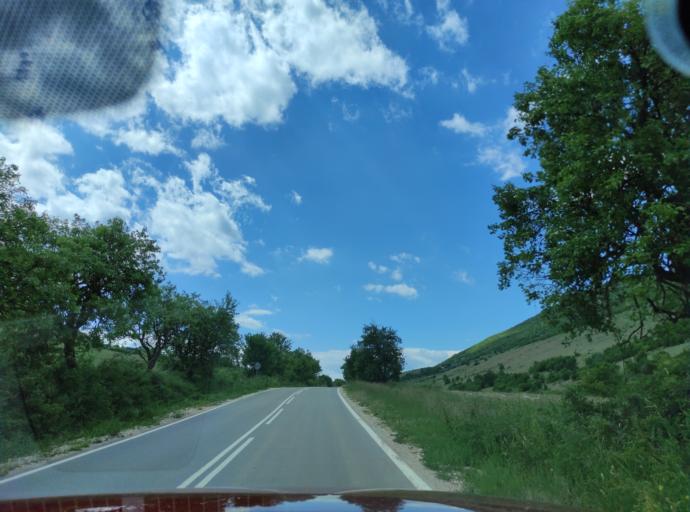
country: BG
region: Montana
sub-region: Obshtina Chiprovtsi
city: Chiprovtsi
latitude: 43.4742
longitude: 22.8452
